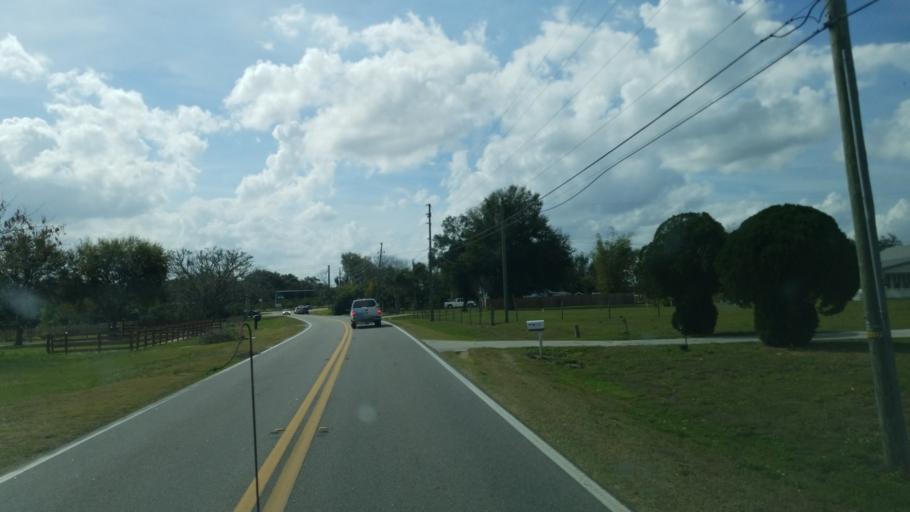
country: US
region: Florida
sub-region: Polk County
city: Lake Wales
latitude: 27.9603
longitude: -81.5924
